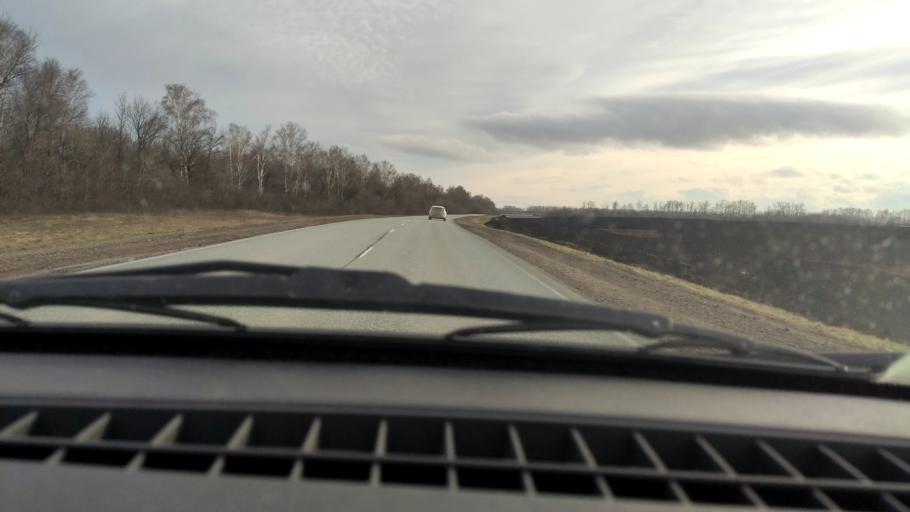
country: RU
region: Bashkortostan
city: Chishmy
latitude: 54.5044
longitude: 55.2873
